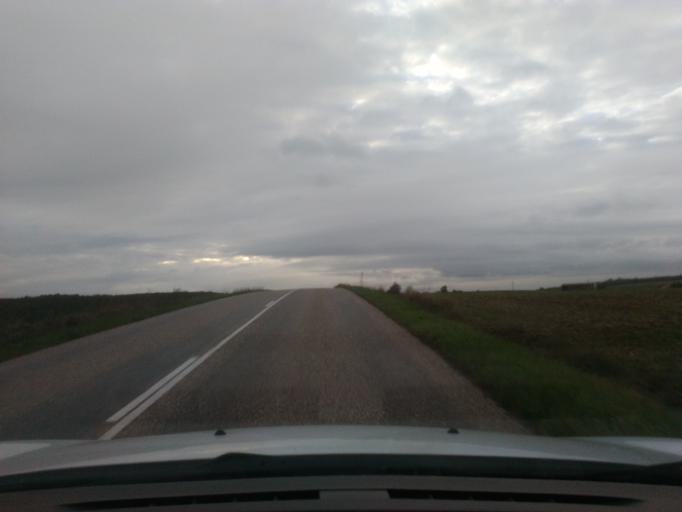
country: FR
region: Lorraine
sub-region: Departement des Vosges
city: Rambervillers
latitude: 48.3502
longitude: 6.5263
